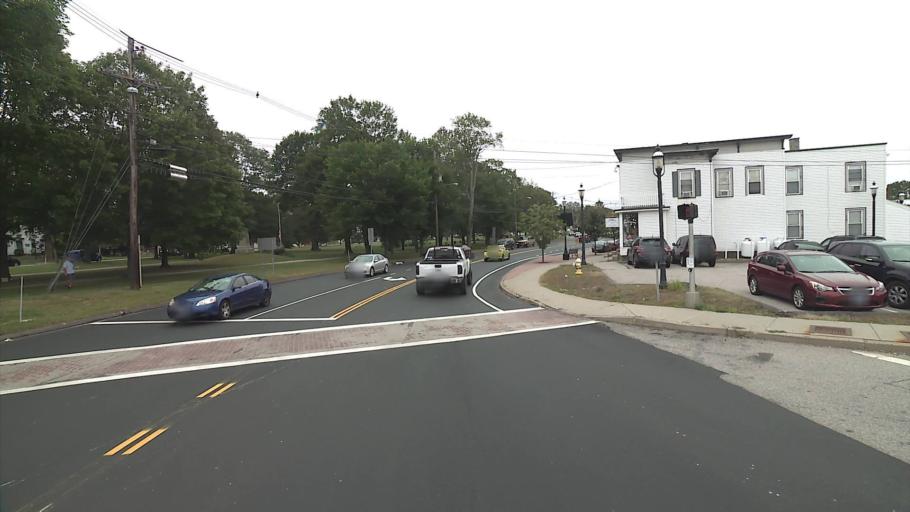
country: US
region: Connecticut
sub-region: New London County
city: Colchester
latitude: 41.5758
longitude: -72.3324
